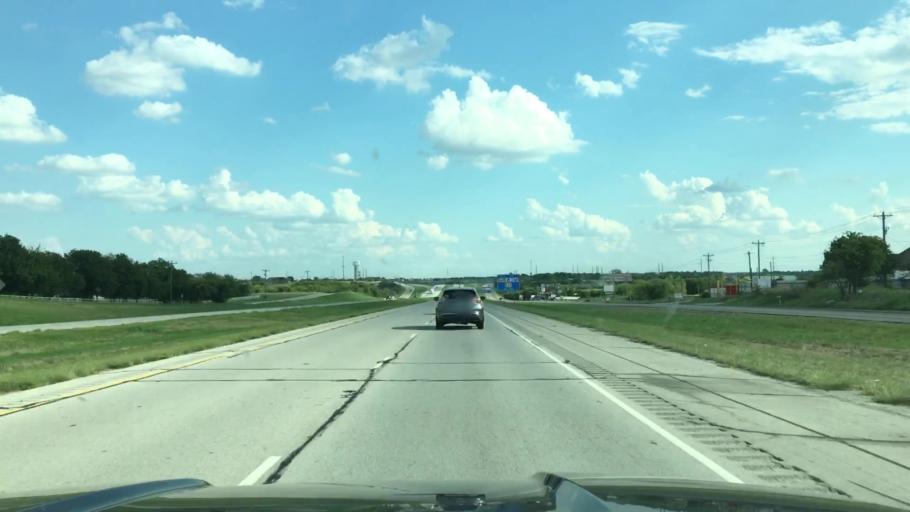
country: US
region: Texas
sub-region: Tarrant County
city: Pecan Acres
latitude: 32.9844
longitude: -97.4275
